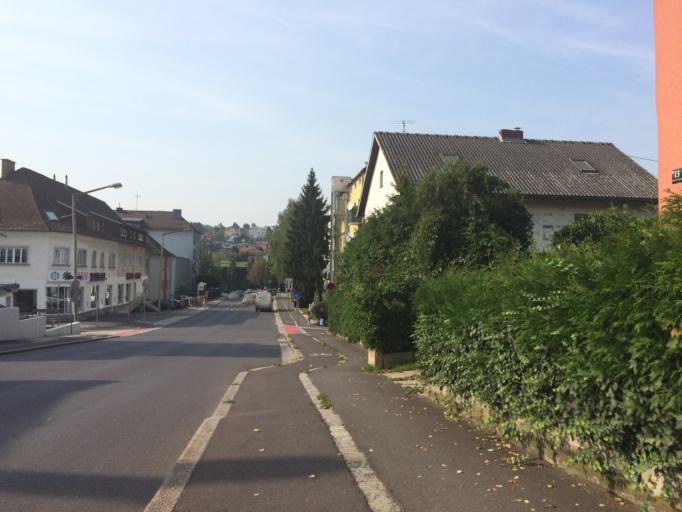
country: AT
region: Upper Austria
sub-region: Politischer Bezirk Linz-Land
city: Leonding
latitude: 48.2762
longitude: 14.2784
